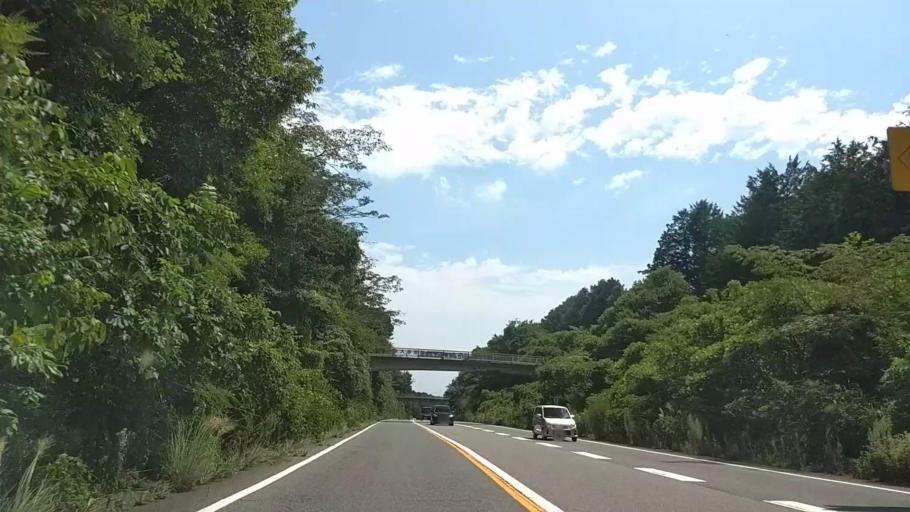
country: JP
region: Shizuoka
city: Fujinomiya
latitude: 35.2922
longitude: 138.6079
